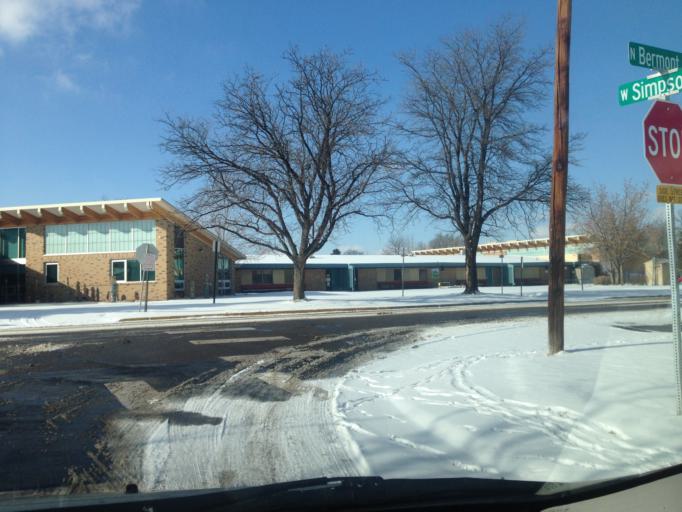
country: US
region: Colorado
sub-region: Boulder County
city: Lafayette
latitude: 39.9983
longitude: -105.0955
